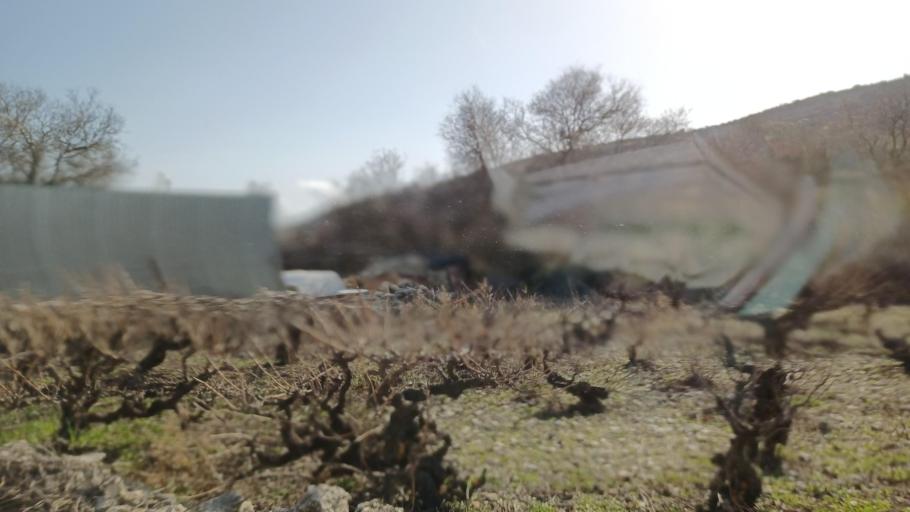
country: CY
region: Limassol
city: Pachna
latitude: 34.8459
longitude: 32.8124
